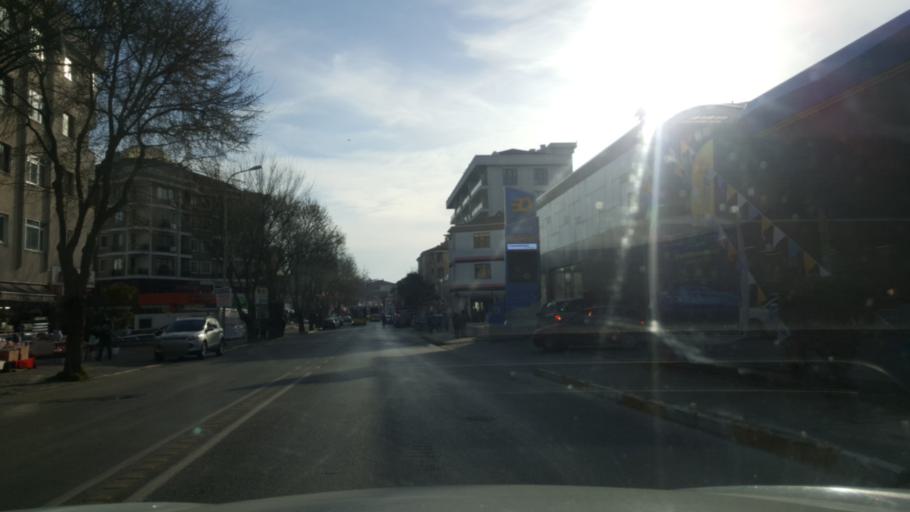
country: TR
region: Istanbul
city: Icmeler
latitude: 40.8196
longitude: 29.3066
